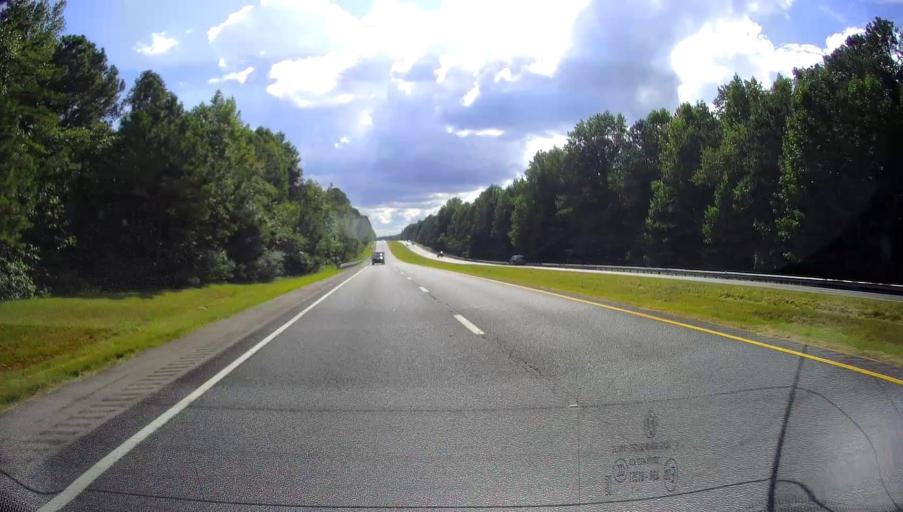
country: US
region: Georgia
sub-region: Muscogee County
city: Columbus
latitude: 32.5610
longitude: -84.8365
